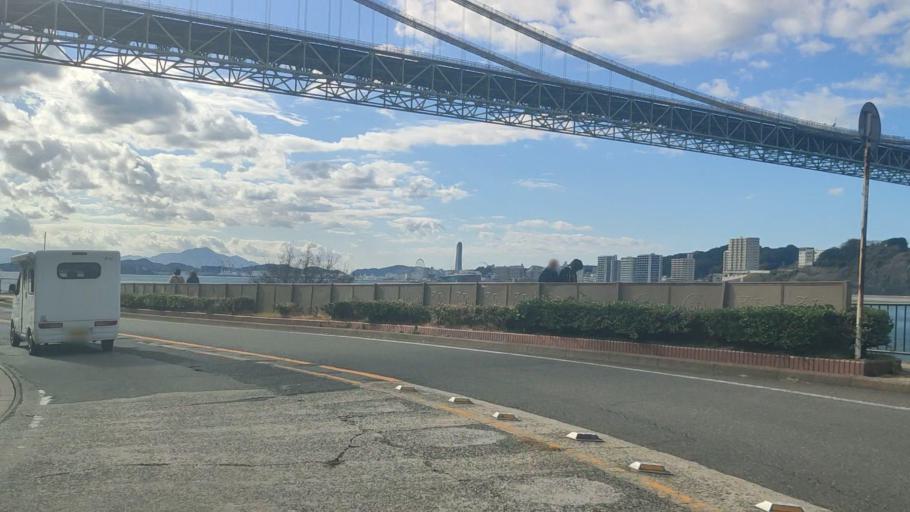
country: JP
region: Yamaguchi
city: Shimonoseki
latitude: 33.9619
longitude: 130.9631
